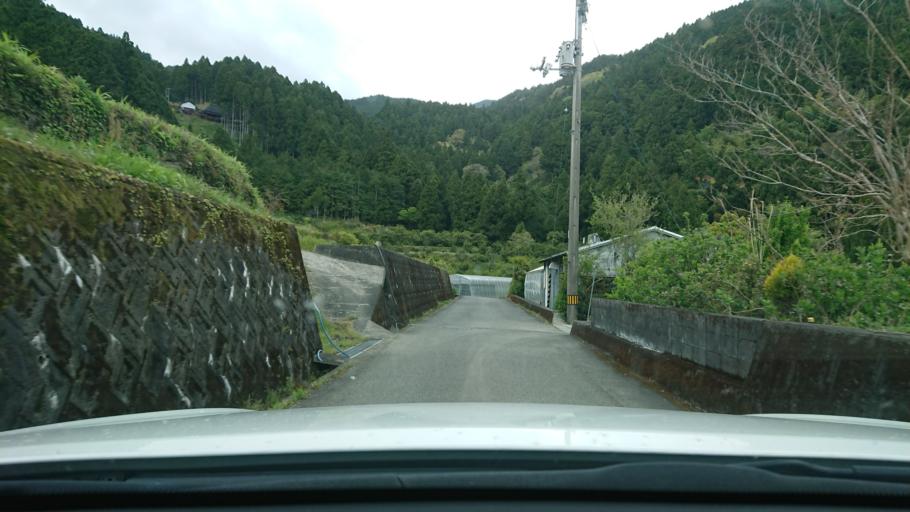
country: JP
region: Tokushima
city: Kamojimacho-jogejima
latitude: 33.8865
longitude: 134.3922
